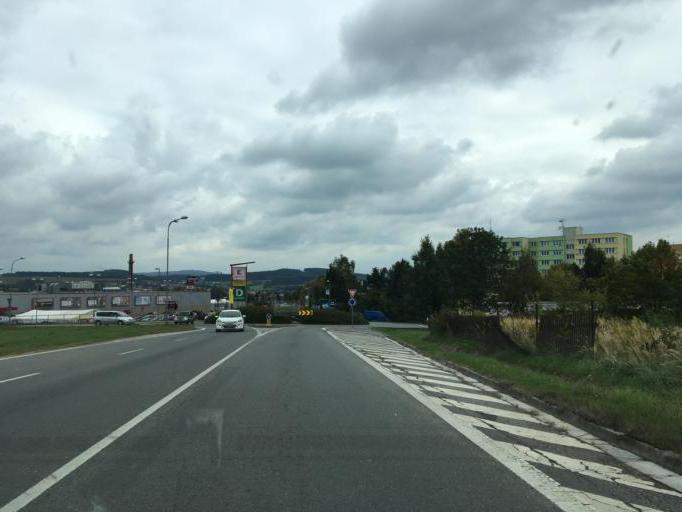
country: CZ
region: Vysocina
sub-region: Okres Pelhrimov
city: Pelhrimov
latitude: 49.4397
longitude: 15.2088
